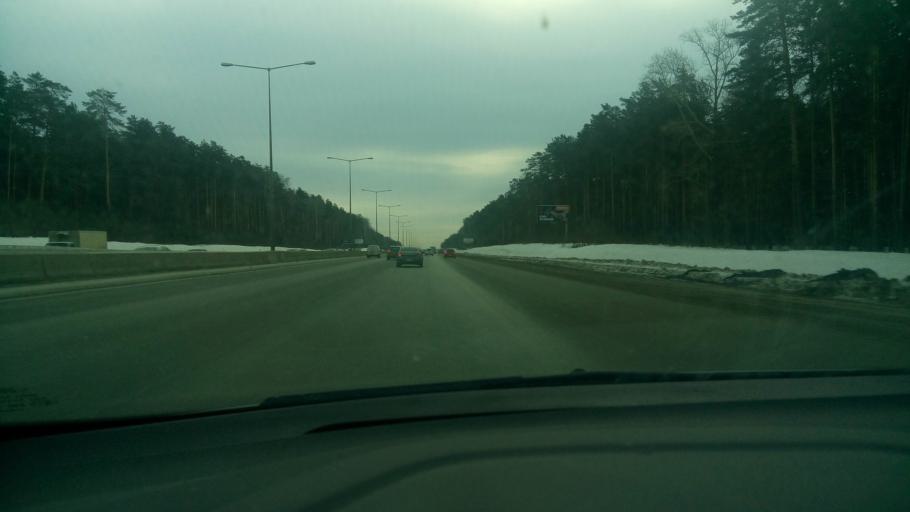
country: RU
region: Sverdlovsk
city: Yekaterinburg
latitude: 56.7875
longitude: 60.6801
